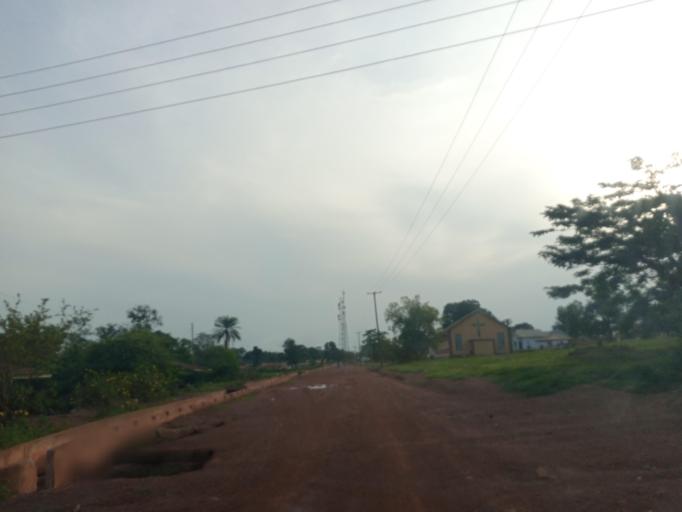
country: SL
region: Southern Province
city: Largo
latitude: 8.1135
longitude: -12.0682
